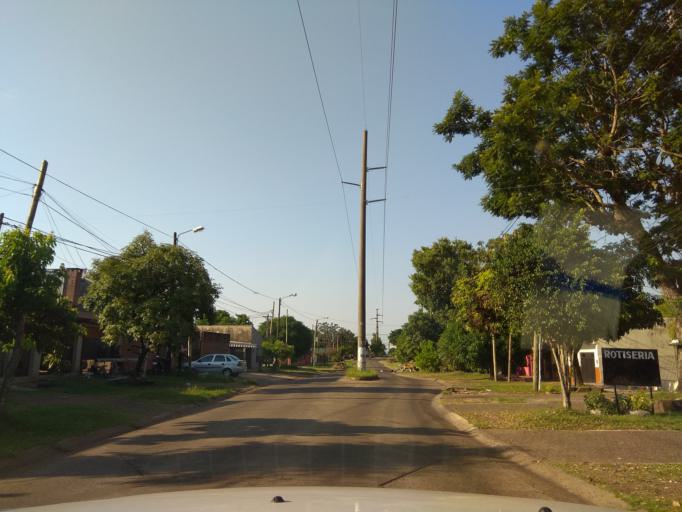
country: AR
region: Misiones
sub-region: Departamento de Capital
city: Posadas
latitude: -27.3683
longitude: -55.9129
